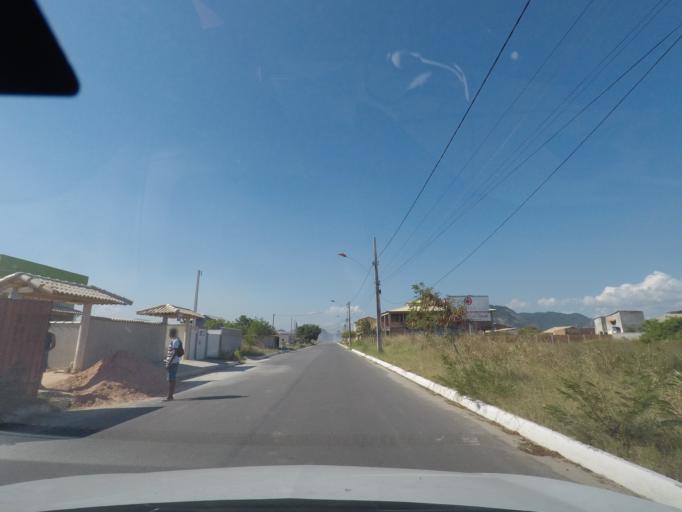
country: BR
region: Rio de Janeiro
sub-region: Marica
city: Marica
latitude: -22.9635
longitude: -42.9271
